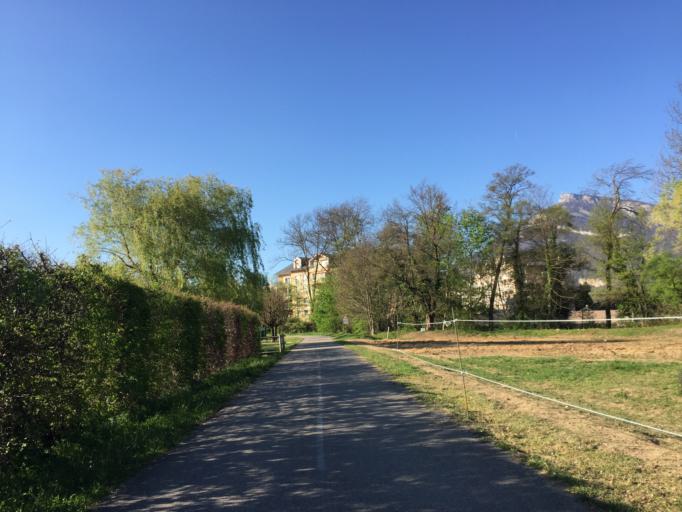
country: FR
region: Rhone-Alpes
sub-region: Departement de la Savoie
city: Chambery
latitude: 45.5598
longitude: 5.9456
